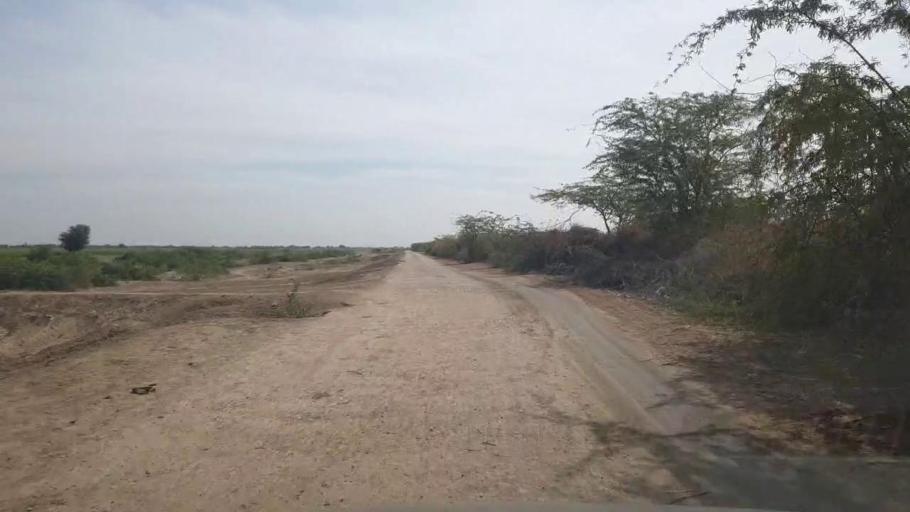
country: PK
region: Sindh
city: Kunri
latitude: 25.2720
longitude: 69.5992
